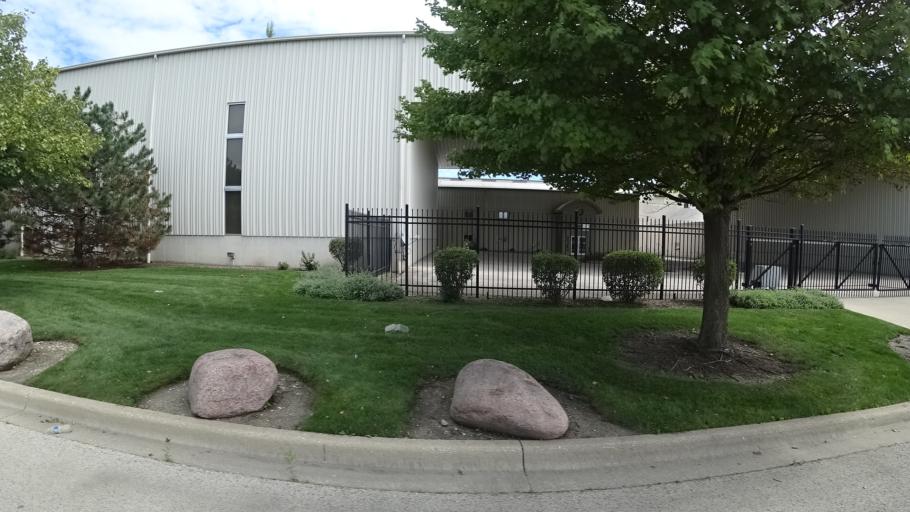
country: US
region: Illinois
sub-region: Cook County
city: Chicago Ridge
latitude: 41.7091
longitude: -87.7891
